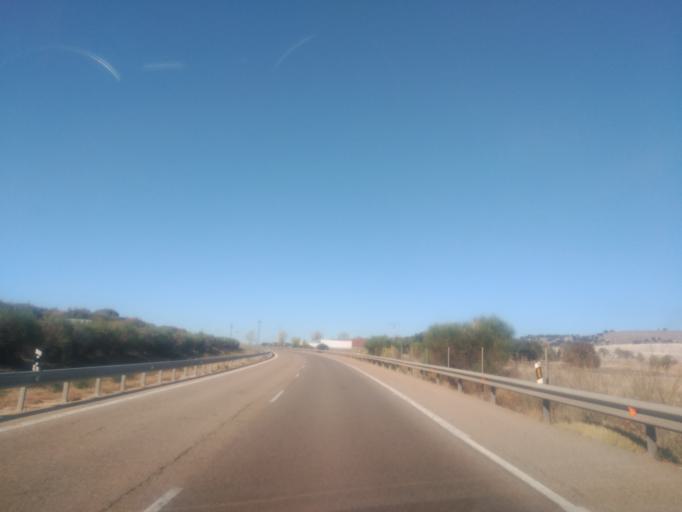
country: ES
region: Castille and Leon
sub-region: Provincia de Valladolid
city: Tudela de Duero
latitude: 41.5962
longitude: -4.6256
